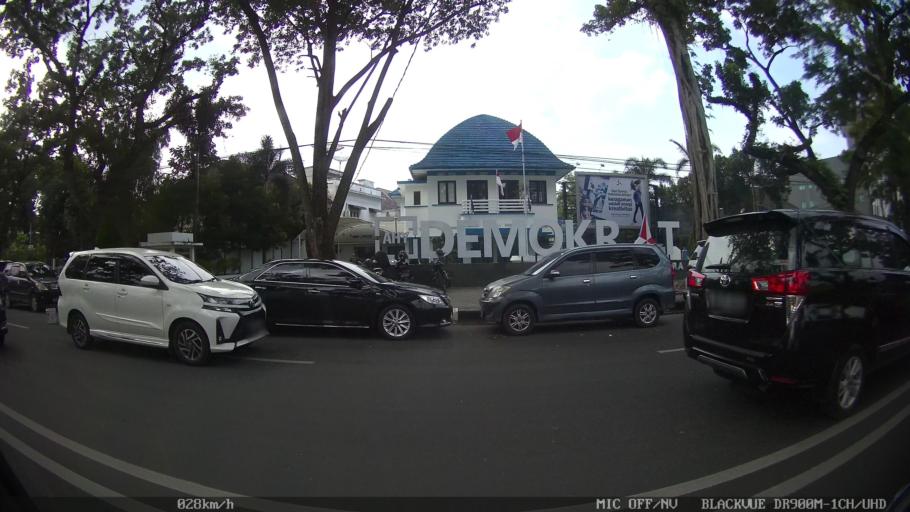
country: ID
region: North Sumatra
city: Medan
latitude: 3.5762
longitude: 98.6750
